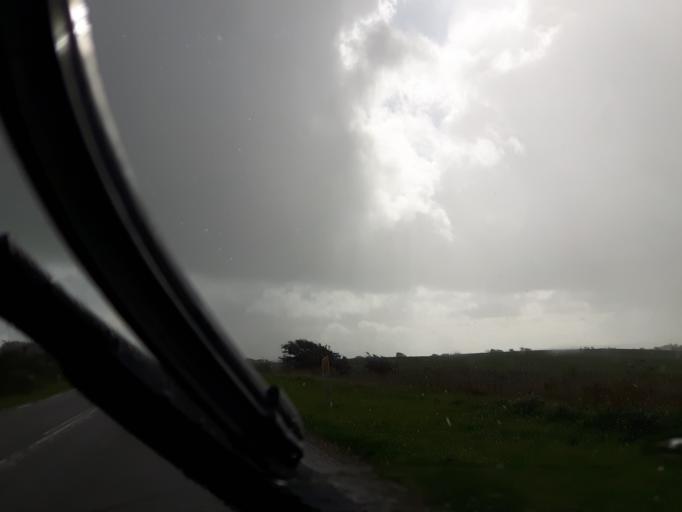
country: DK
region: North Denmark
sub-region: Thisted Kommune
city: Hurup
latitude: 56.6332
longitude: 8.5122
